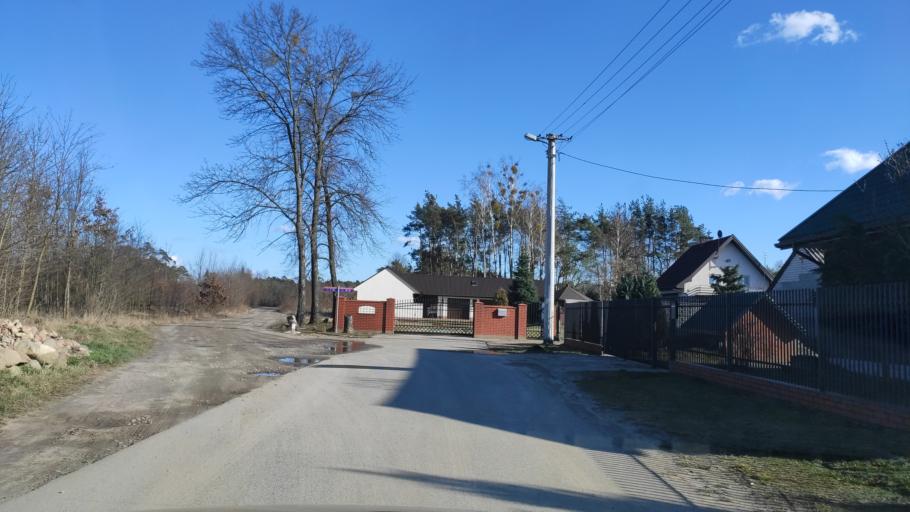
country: PL
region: Masovian Voivodeship
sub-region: Powiat radomski
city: Jastrzebia
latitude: 51.4556
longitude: 21.2721
